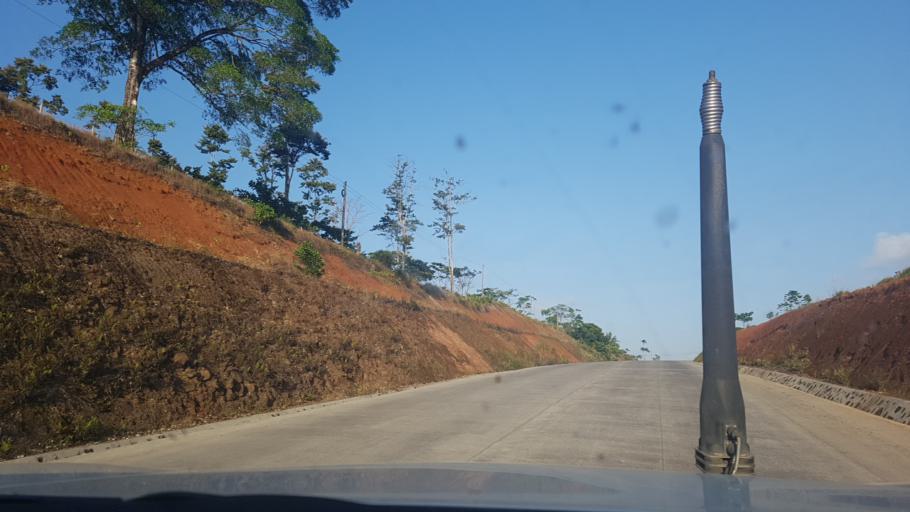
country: NI
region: Atlantico Sur
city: Nueva Guinea
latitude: 11.8065
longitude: -84.1164
